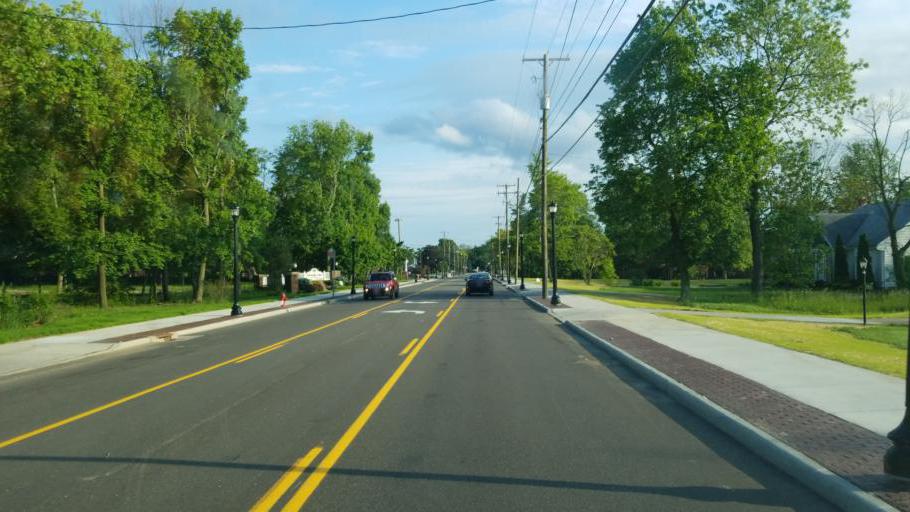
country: US
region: Ohio
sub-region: Summit County
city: Tallmadge
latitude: 41.1065
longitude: -81.4408
